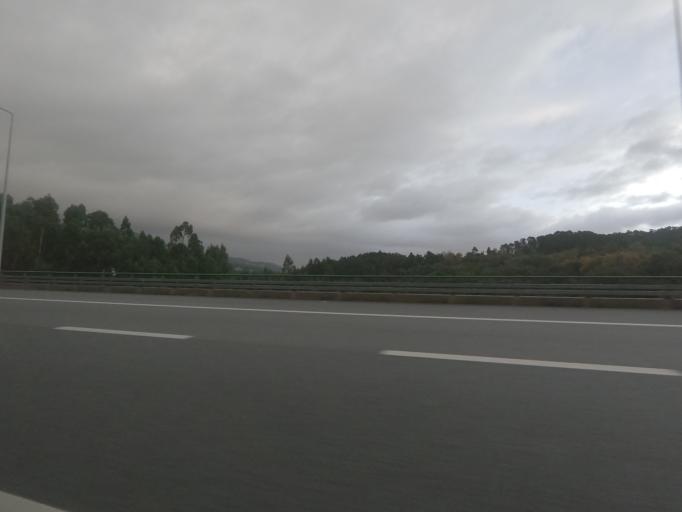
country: PT
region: Viana do Castelo
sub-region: Ponte de Lima
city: Ponte de Lima
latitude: 41.7743
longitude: -8.5583
